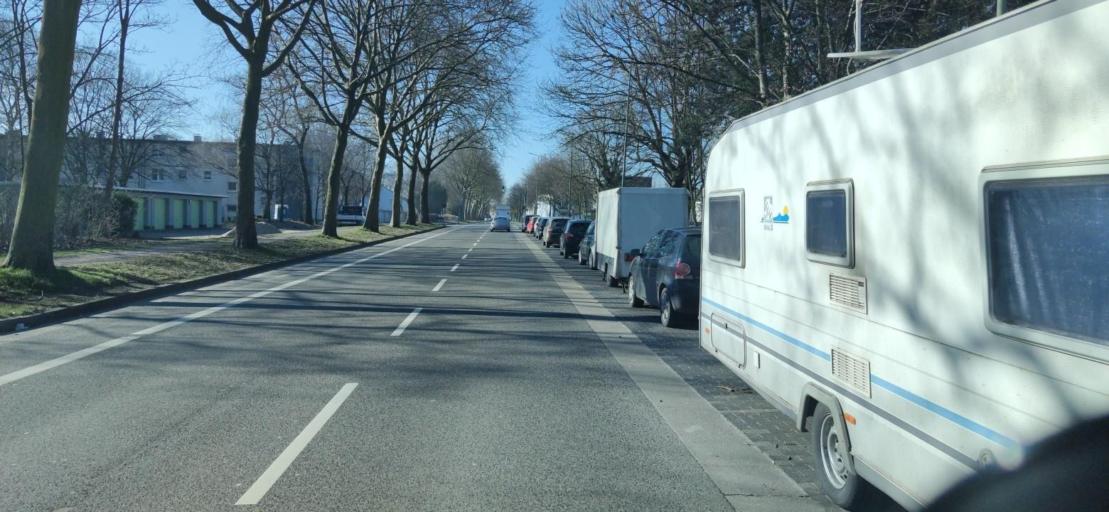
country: DE
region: North Rhine-Westphalia
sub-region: Regierungsbezirk Dusseldorf
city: Dinslaken
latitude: 51.5332
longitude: 6.7474
